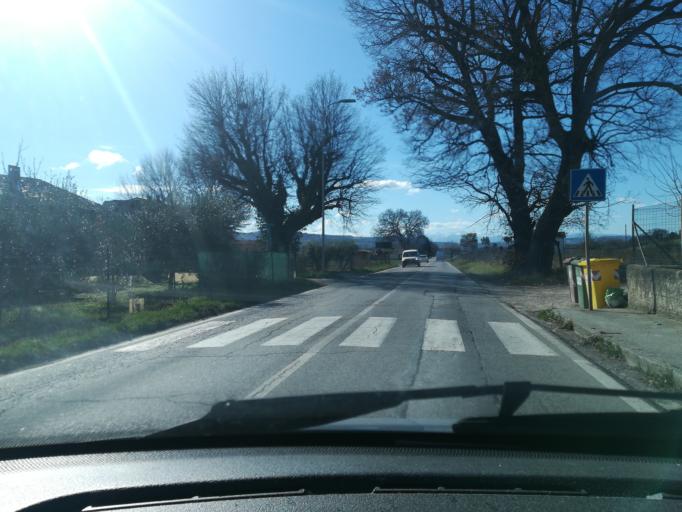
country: IT
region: The Marches
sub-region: Provincia di Macerata
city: Montecassiano
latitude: 43.3445
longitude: 13.4328
